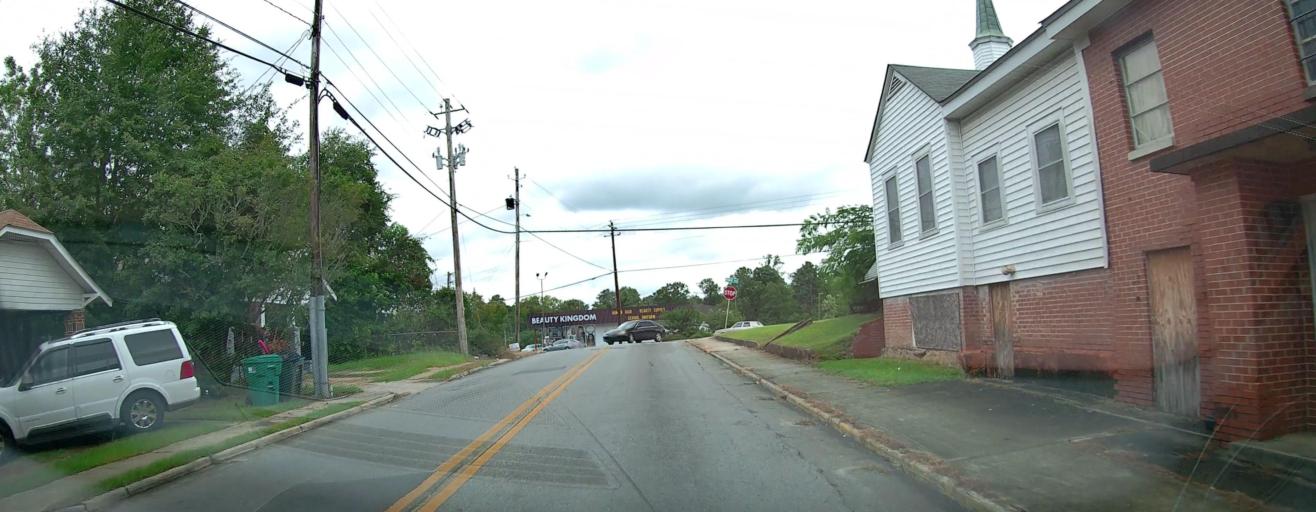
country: US
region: Georgia
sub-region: Bibb County
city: Macon
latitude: 32.8407
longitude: -83.6866
